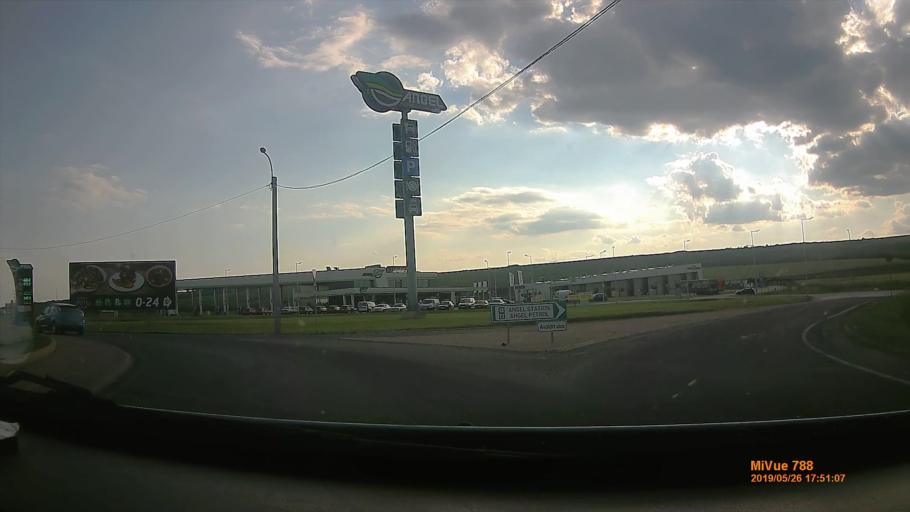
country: HU
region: Borsod-Abauj-Zemplen
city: Szikszo
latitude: 48.1769
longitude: 20.9158
